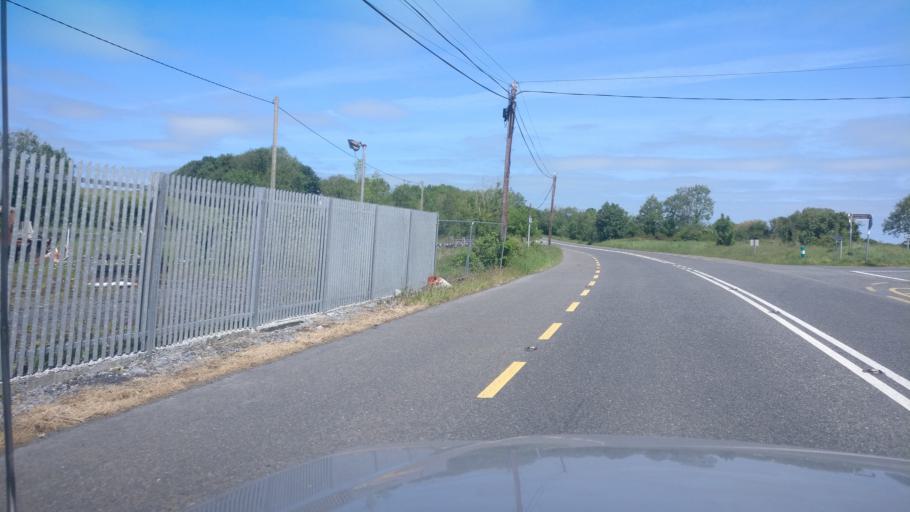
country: IE
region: Connaught
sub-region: County Galway
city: Gort
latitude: 53.1174
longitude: -8.7931
